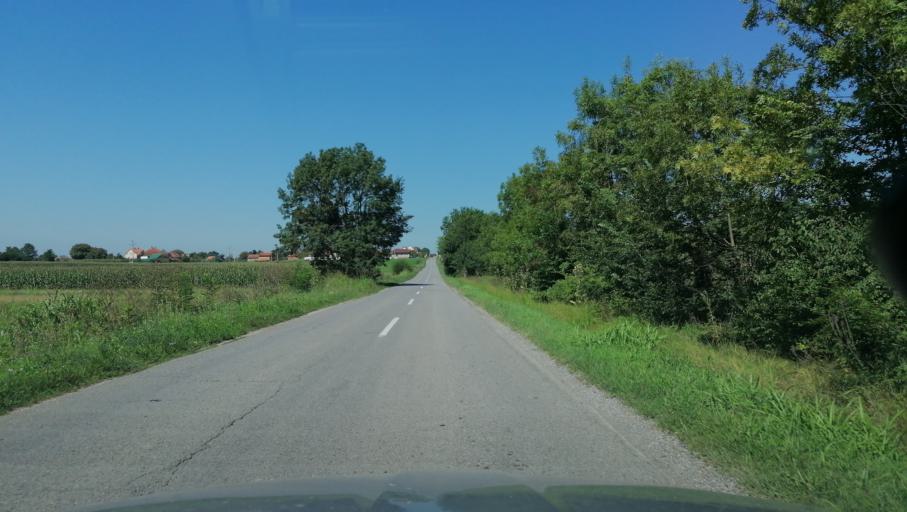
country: RS
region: Central Serbia
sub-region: Raski Okrug
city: Vrnjacka Banja
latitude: 43.6845
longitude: 20.8836
